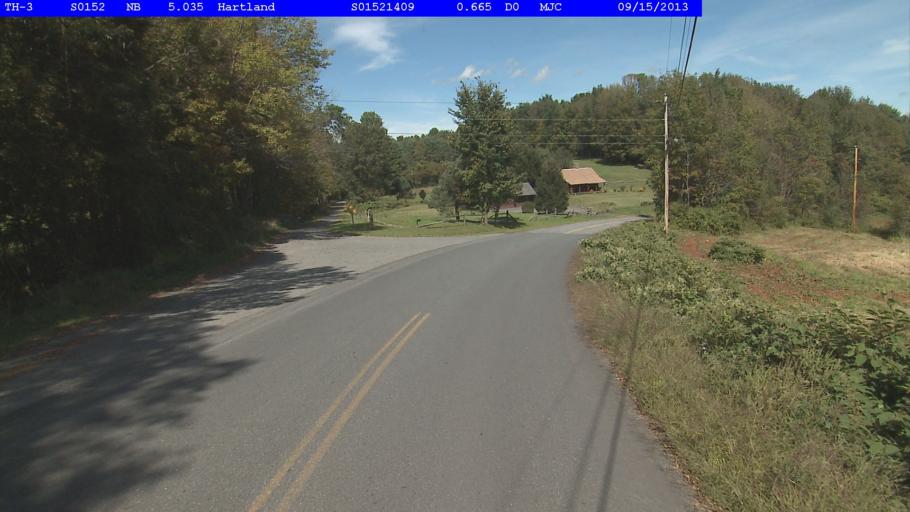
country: US
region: Vermont
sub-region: Windsor County
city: Windsor
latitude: 43.5321
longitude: -72.4379
